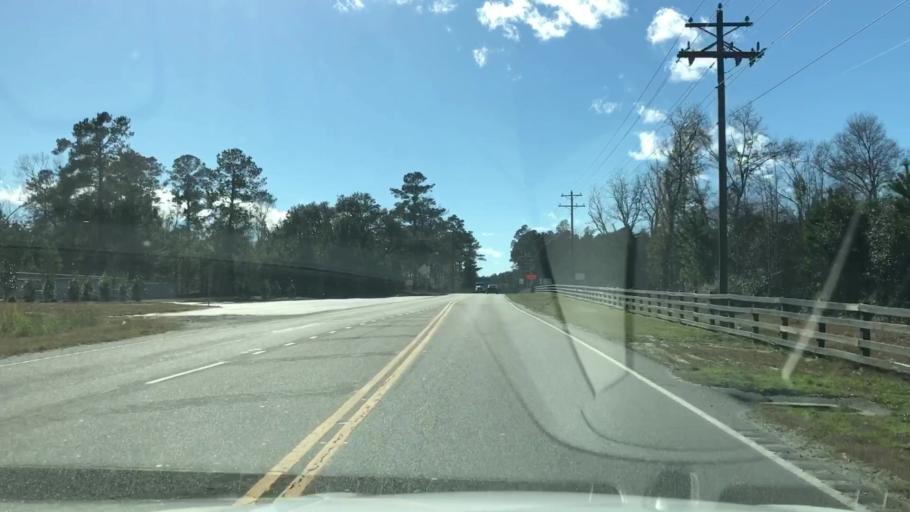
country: US
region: South Carolina
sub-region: Dorchester County
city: Summerville
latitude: 33.0793
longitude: -80.2111
